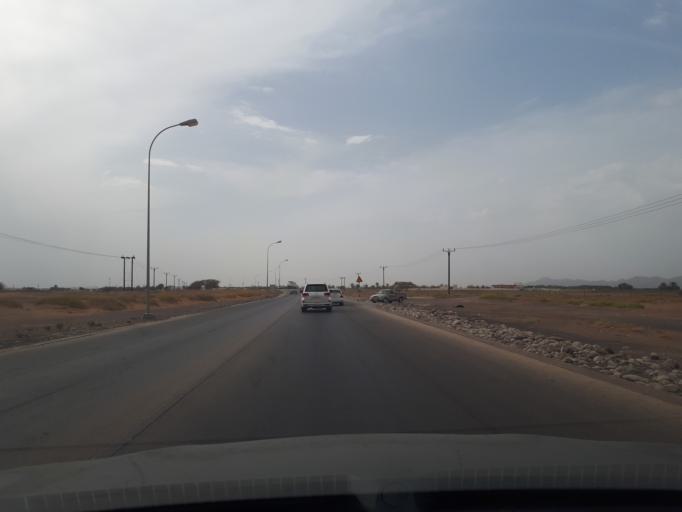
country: OM
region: Ash Sharqiyah
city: Badiyah
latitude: 22.4846
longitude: 58.7763
